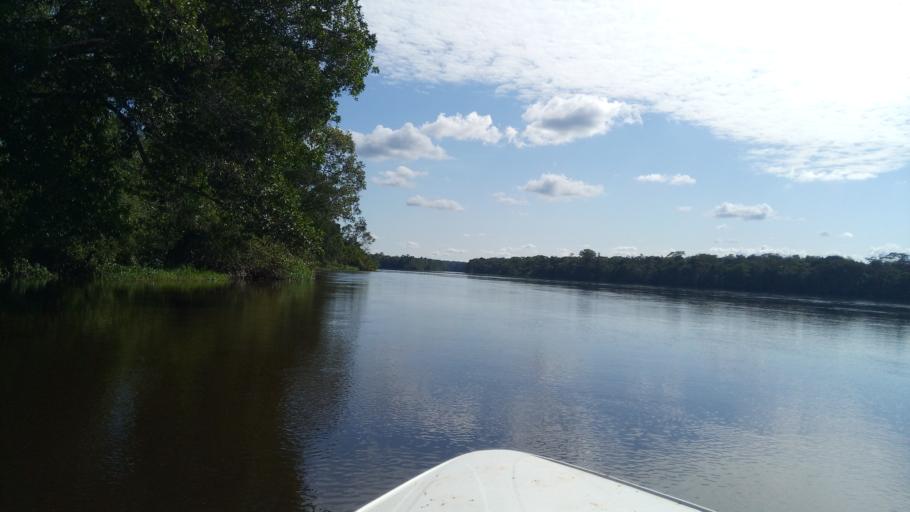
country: CD
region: Eastern Province
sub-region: Sous-Region de la Tshopo
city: Yangambi
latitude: 0.5328
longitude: 24.1978
